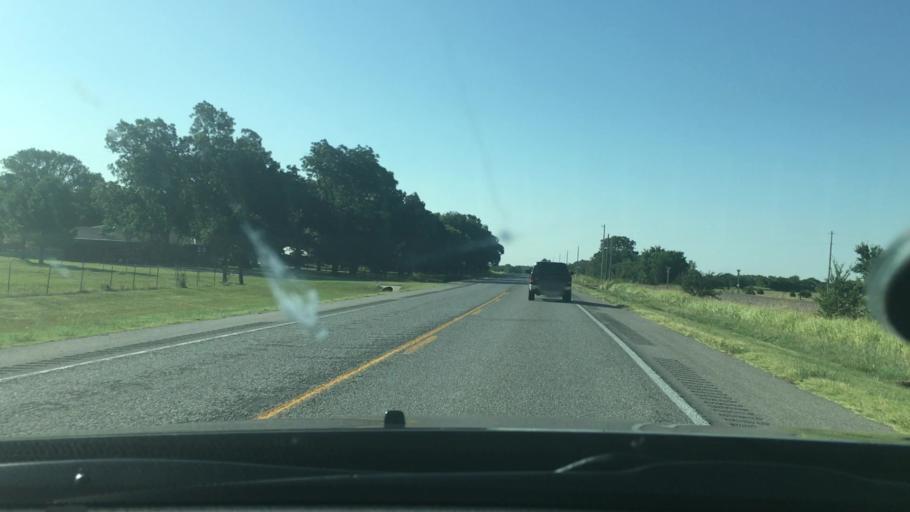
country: US
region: Oklahoma
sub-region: Johnston County
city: Tishomingo
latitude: 34.2610
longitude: -96.7695
